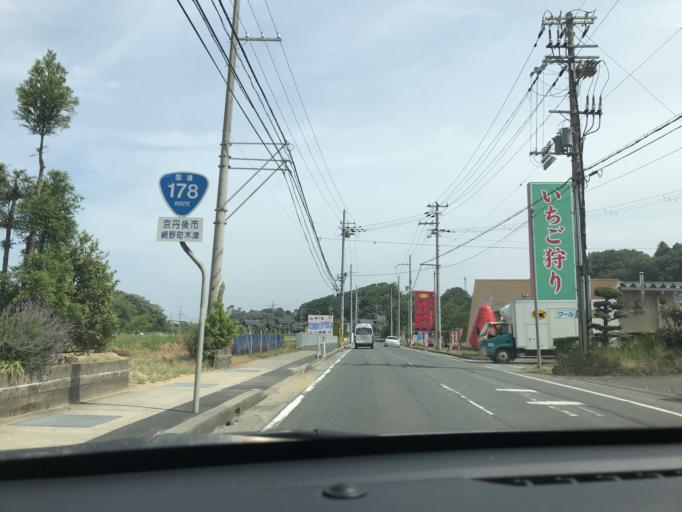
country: JP
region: Hyogo
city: Toyooka
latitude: 35.6517
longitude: 134.9699
